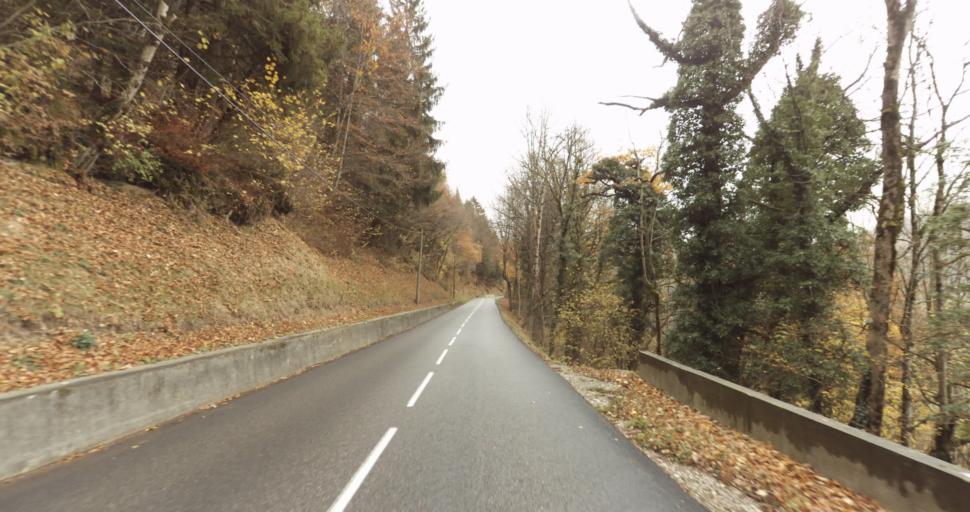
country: FR
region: Rhone-Alpes
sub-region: Departement de la Haute-Savoie
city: Thorens-Glieres
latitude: 45.9878
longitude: 6.2717
